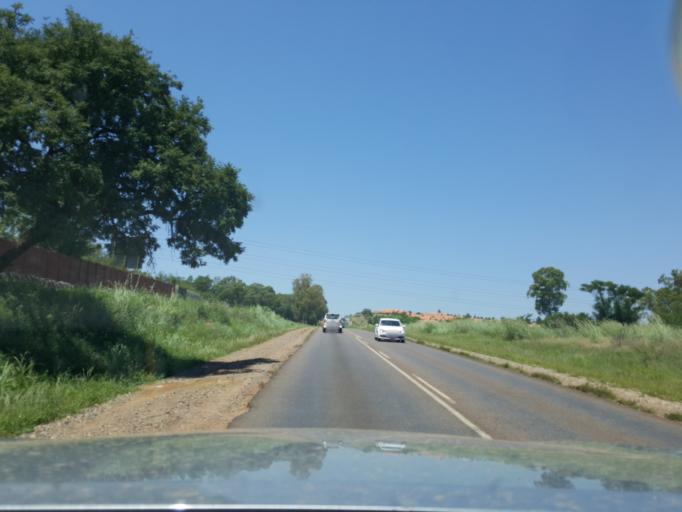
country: ZA
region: Gauteng
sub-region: City of Tshwane Metropolitan Municipality
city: Centurion
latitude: -25.8341
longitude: 28.3209
